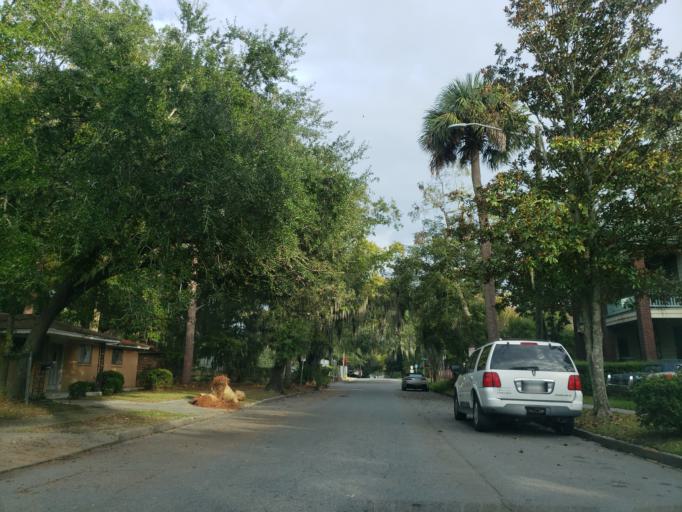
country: US
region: Georgia
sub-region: Chatham County
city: Savannah
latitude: 32.0603
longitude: -81.0798
